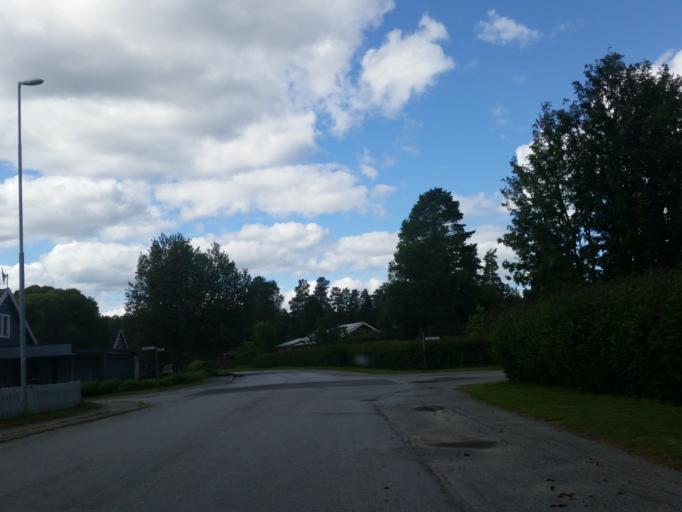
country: SE
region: Vaesterbotten
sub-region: Robertsfors Kommun
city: Robertsfors
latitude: 64.1982
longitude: 20.8466
